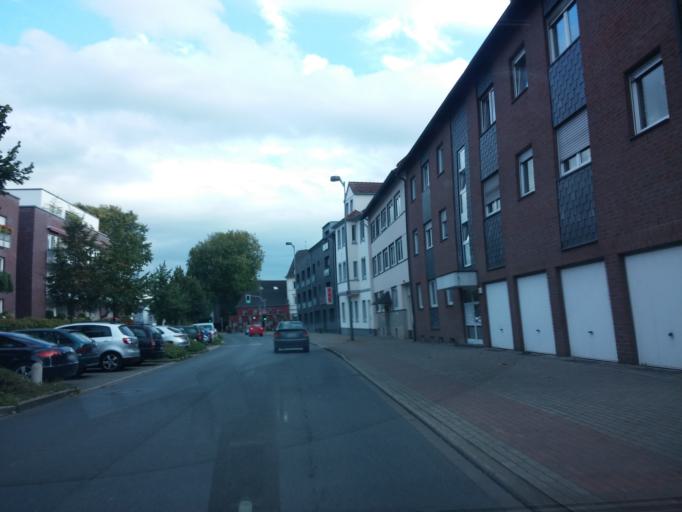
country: DE
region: North Rhine-Westphalia
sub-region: Regierungsbezirk Munster
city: Gladbeck
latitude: 51.5818
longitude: 7.0461
